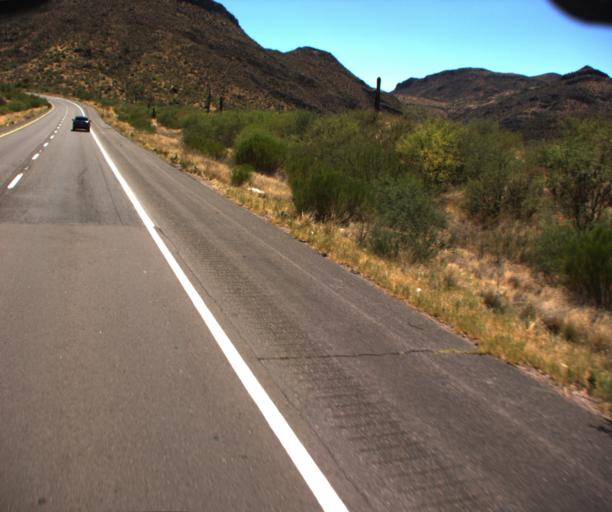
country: US
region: Arizona
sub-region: Maricopa County
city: Rio Verde
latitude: 33.7953
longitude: -111.4937
